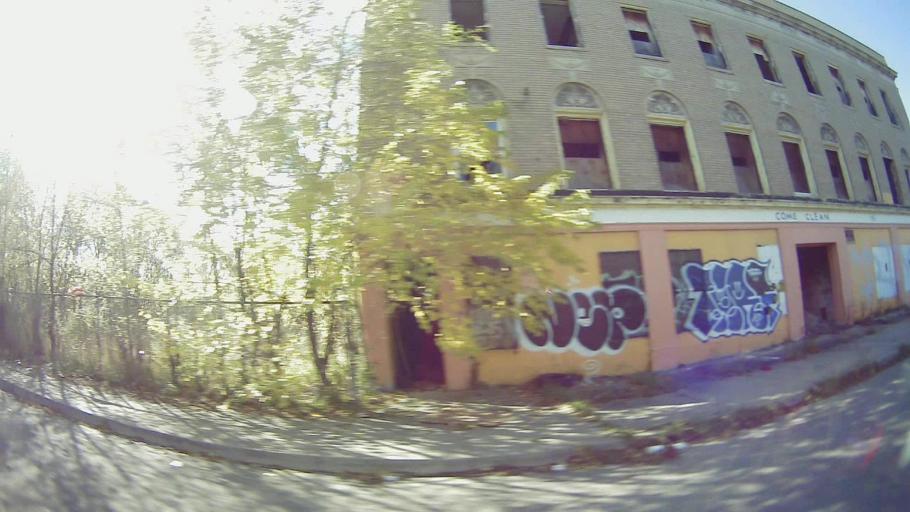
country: US
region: Michigan
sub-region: Wayne County
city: Highland Park
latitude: 42.3576
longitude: -83.0914
